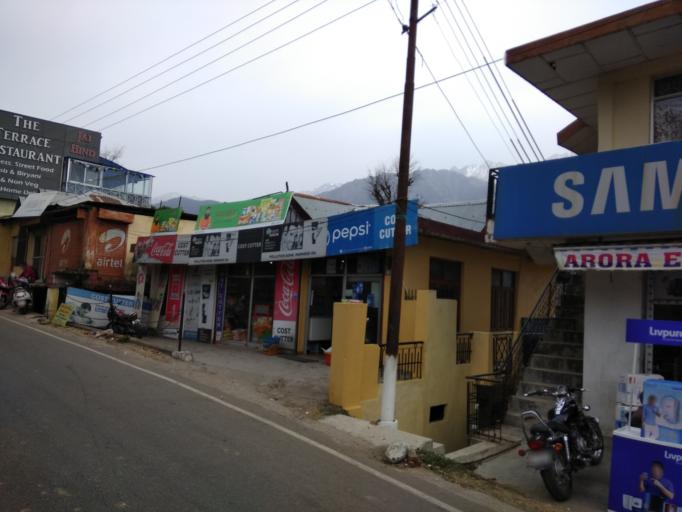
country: IN
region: Himachal Pradesh
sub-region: Kangra
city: Dharmsala
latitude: 32.2052
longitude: 76.3250
